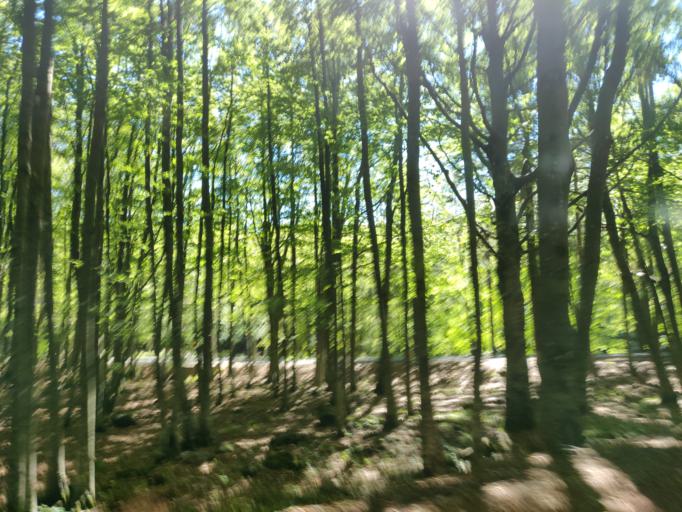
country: IT
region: Tuscany
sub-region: Provincia di Siena
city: Abbadia San Salvatore
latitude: 42.8831
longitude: 11.6229
